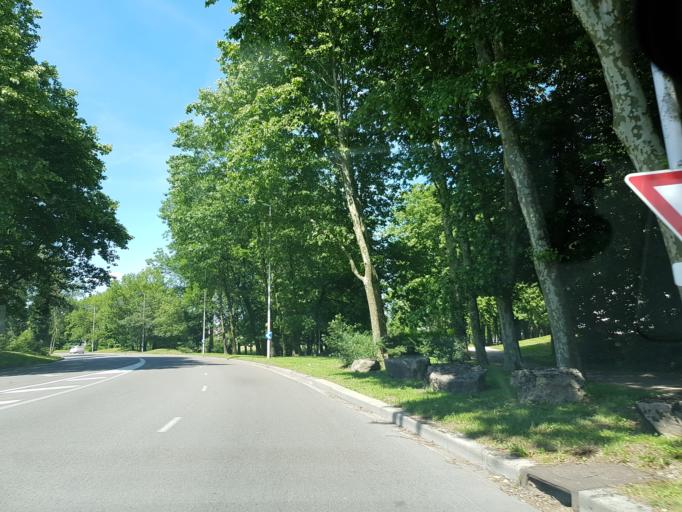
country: FR
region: Rhone-Alpes
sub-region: Departement de l'Ain
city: Bourg-en-Bresse
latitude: 46.2041
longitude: 5.2428
